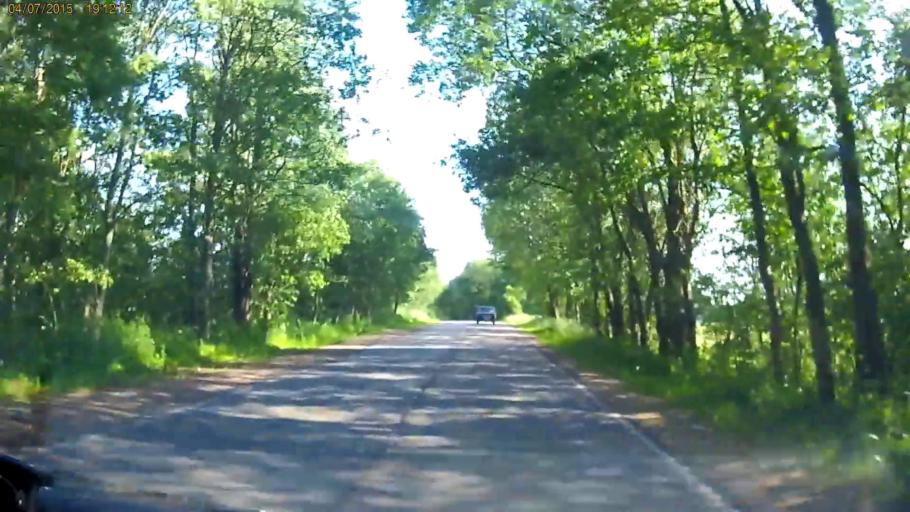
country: RU
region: Leningrad
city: Garbolovo
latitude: 60.3194
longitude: 30.4933
